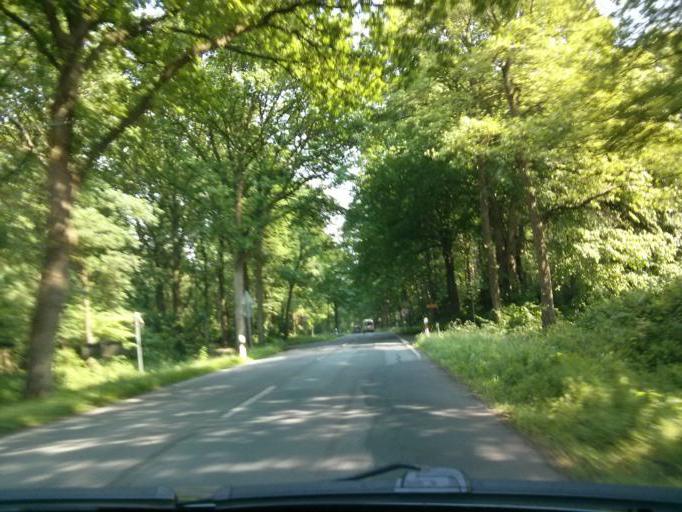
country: DE
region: Lower Saxony
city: Schiffdorf
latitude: 53.5177
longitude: 8.6770
